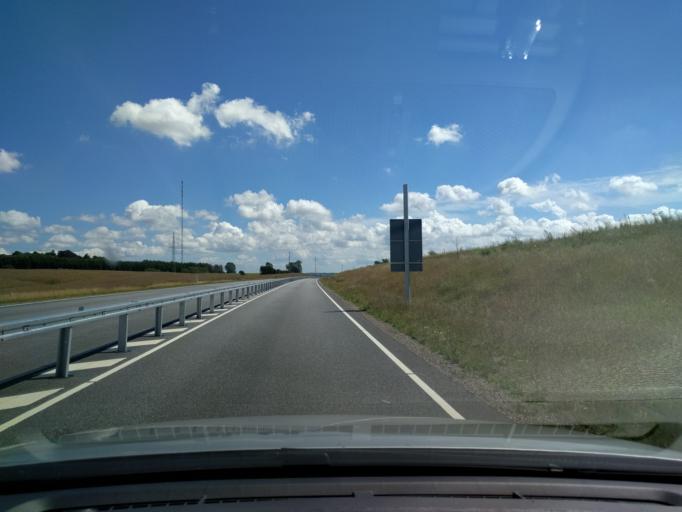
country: DK
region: Zealand
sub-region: Naestved Kommune
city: Fensmark
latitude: 55.2607
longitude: 11.7936
